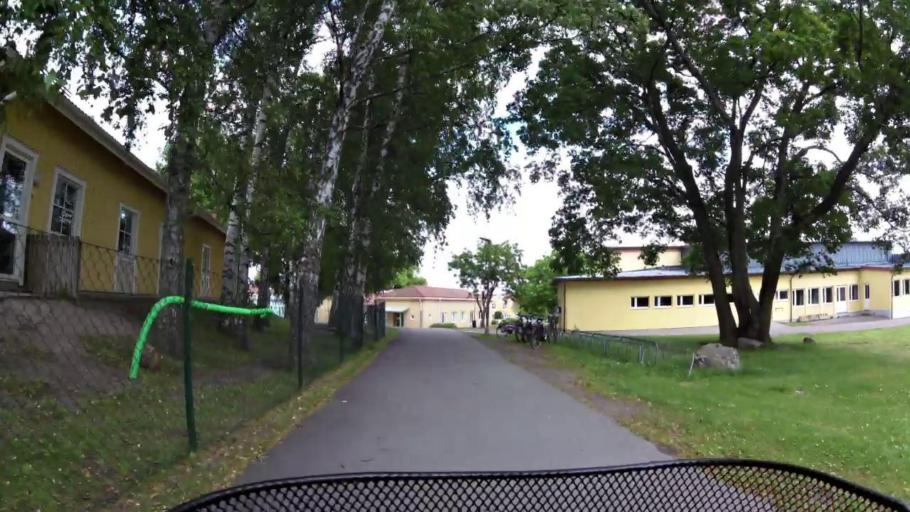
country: SE
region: OEstergoetland
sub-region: Linkopings Kommun
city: Malmslatt
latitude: 58.4164
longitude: 15.5166
